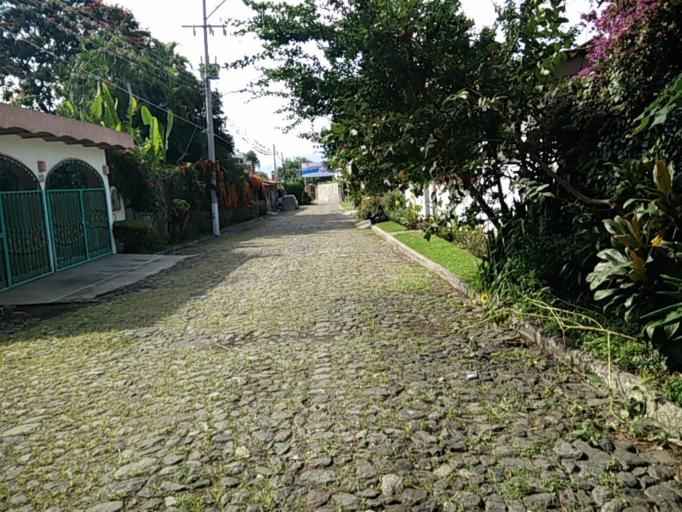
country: MX
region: Jalisco
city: Ajijic
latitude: 20.2986
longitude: -103.2739
